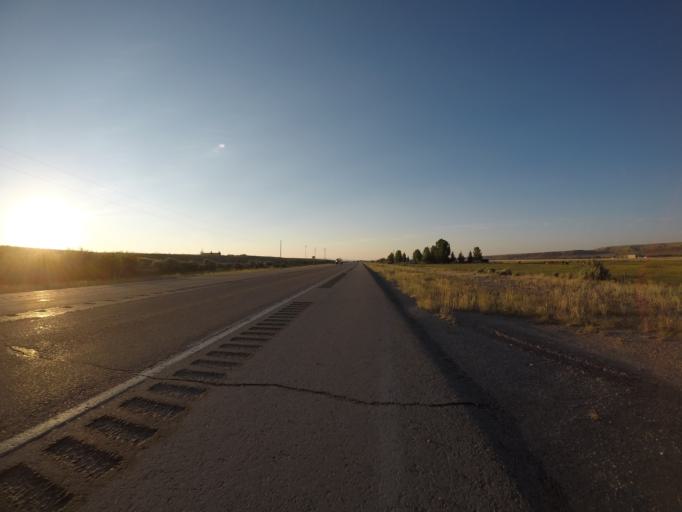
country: US
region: Wyoming
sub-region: Sublette County
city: Pinedale
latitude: 42.8079
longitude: -109.8246
